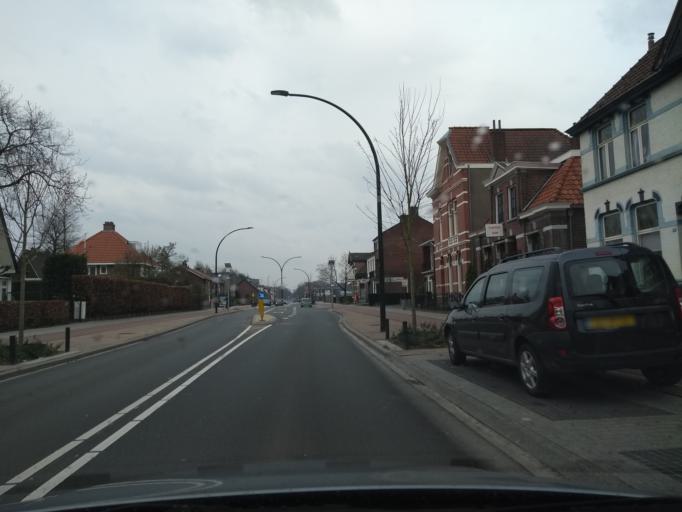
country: NL
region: Overijssel
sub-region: Gemeente Hengelo
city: Hengelo
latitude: 52.2612
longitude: 6.8037
